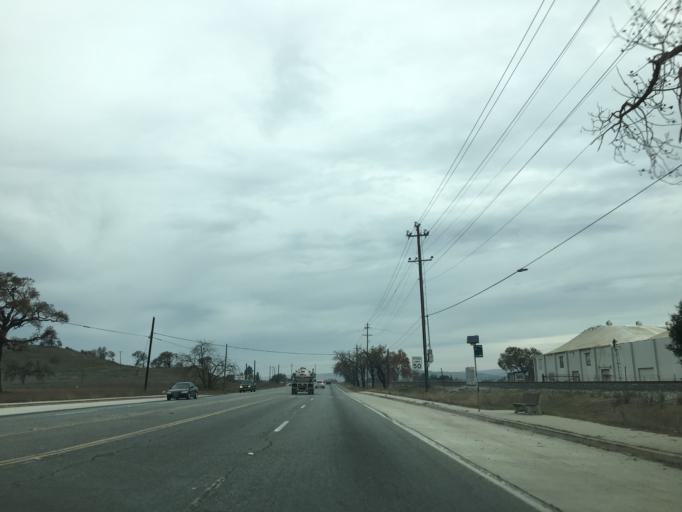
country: US
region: California
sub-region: Santa Clara County
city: San Martin
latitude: 37.0925
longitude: -121.6146
